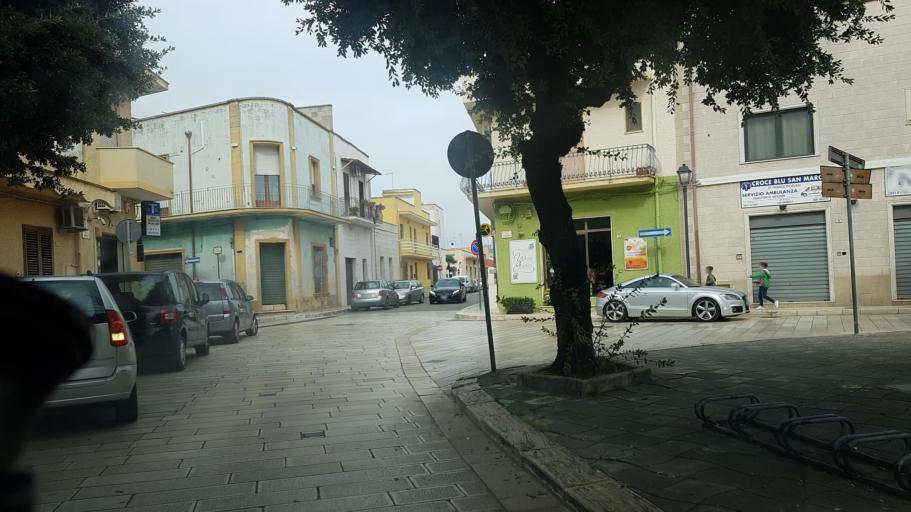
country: IT
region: Apulia
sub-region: Provincia di Brindisi
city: Cellino San Marco
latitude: 40.4719
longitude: 17.9641
